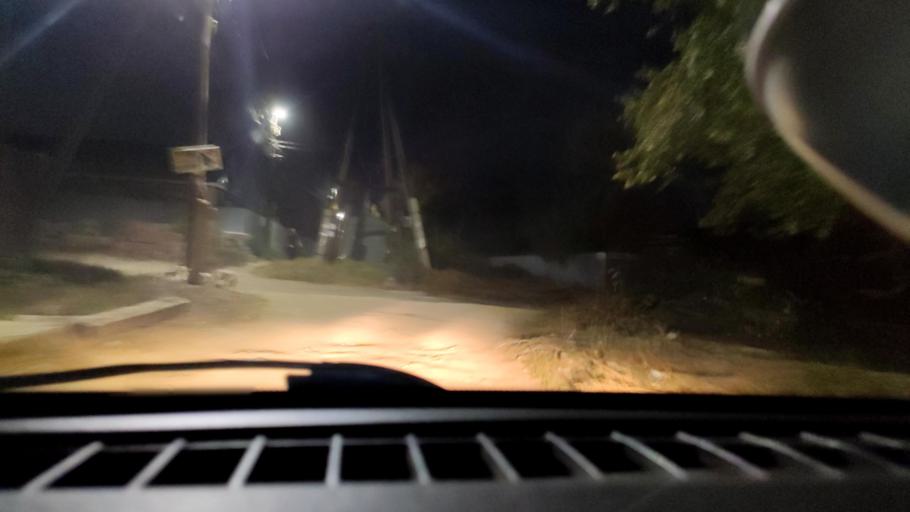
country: RU
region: Samara
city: Samara
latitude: 53.1765
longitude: 50.1720
